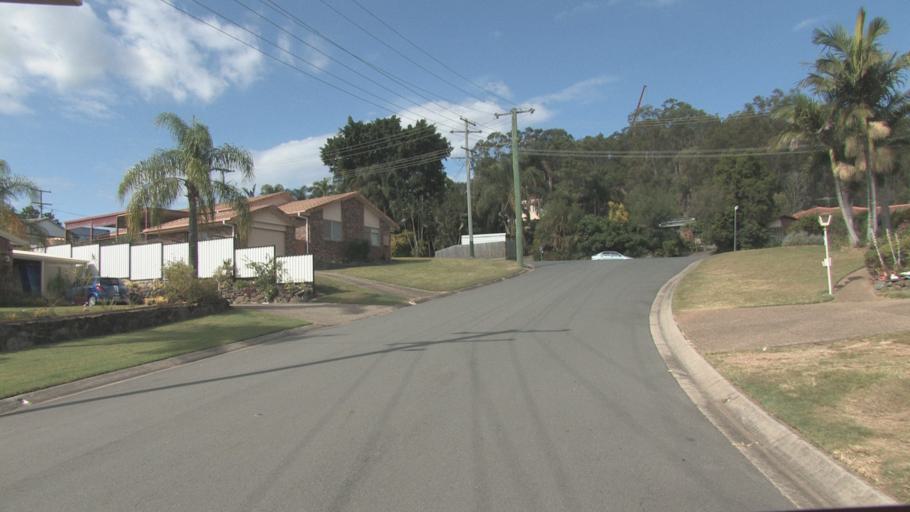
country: AU
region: Queensland
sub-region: Logan
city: Windaroo
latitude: -27.7259
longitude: 153.1959
